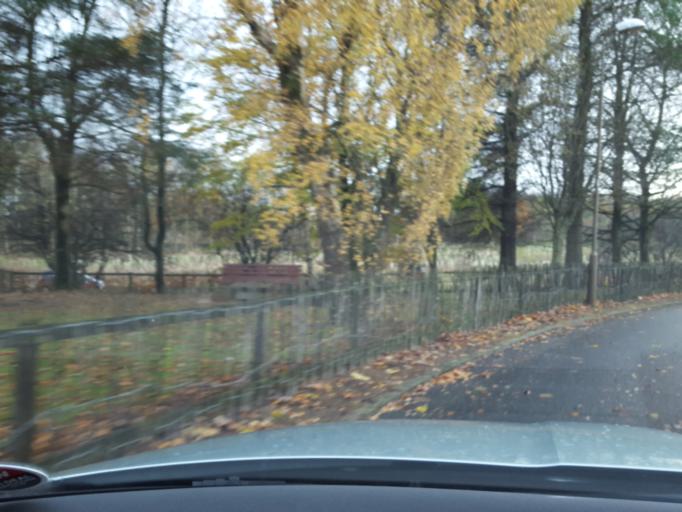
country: GB
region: Scotland
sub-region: West Lothian
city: Livingston
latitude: 55.9205
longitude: -3.5297
